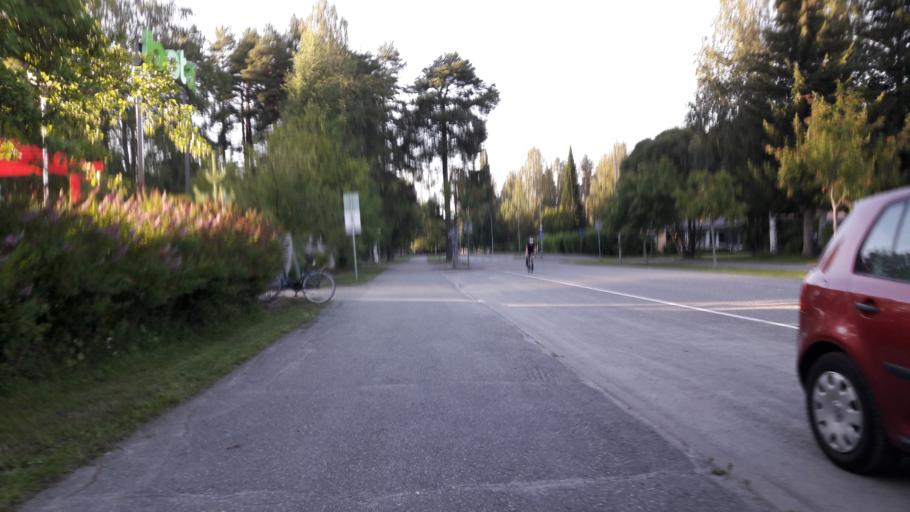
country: FI
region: North Karelia
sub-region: Joensuu
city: Joensuu
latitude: 62.6022
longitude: 29.7248
